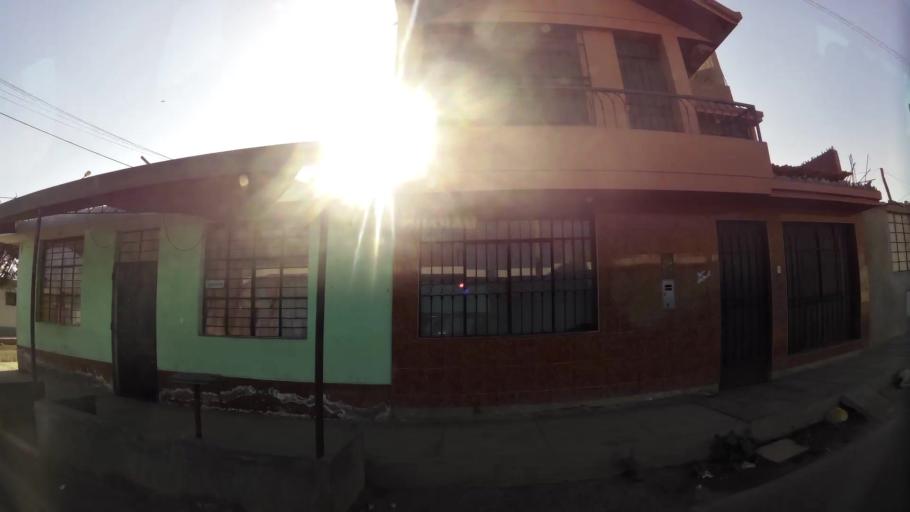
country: PE
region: Ica
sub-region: Provincia de Ica
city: La Tinguina
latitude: -14.0512
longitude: -75.6998
